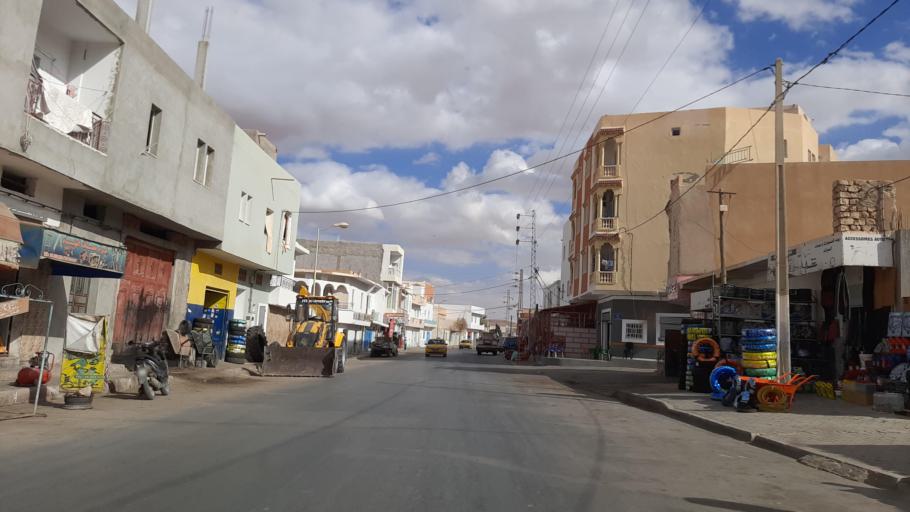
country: TN
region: Tataouine
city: Tataouine
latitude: 32.9255
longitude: 10.4539
